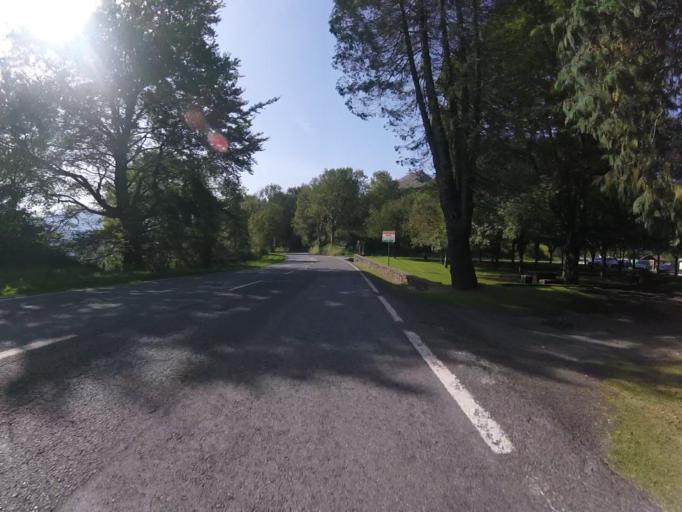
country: ES
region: Navarre
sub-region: Provincia de Navarra
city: Zugarramurdi
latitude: 43.2334
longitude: -1.4981
